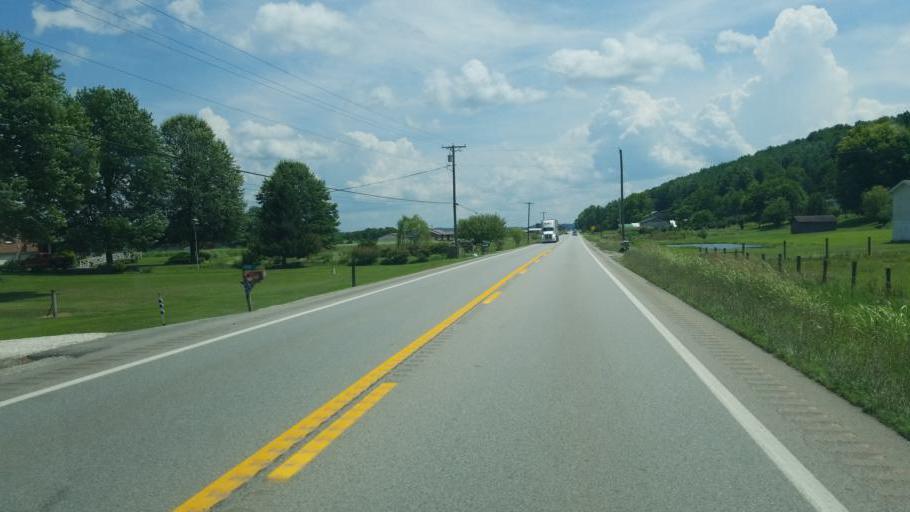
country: US
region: West Virginia
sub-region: Putnam County
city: Buffalo
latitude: 38.7633
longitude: -82.0004
